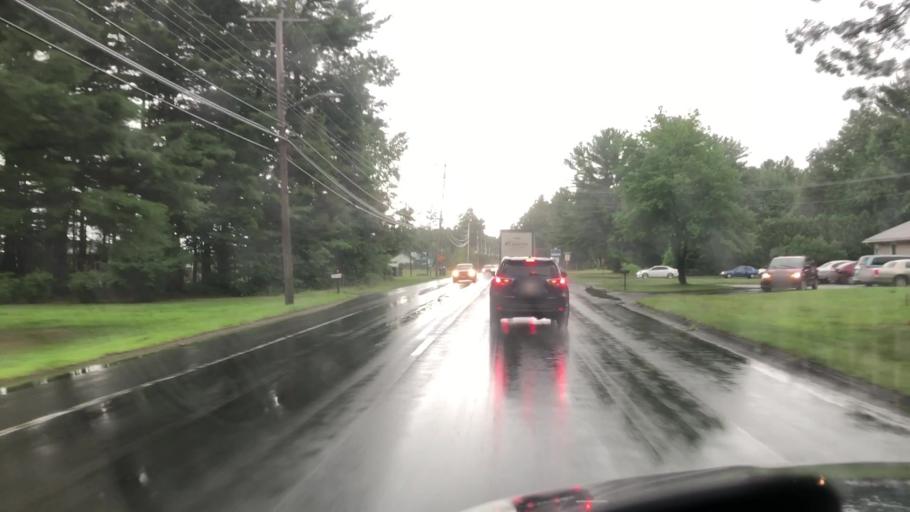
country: US
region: Massachusetts
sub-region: Hampden County
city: Westfield
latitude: 42.1687
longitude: -72.7267
